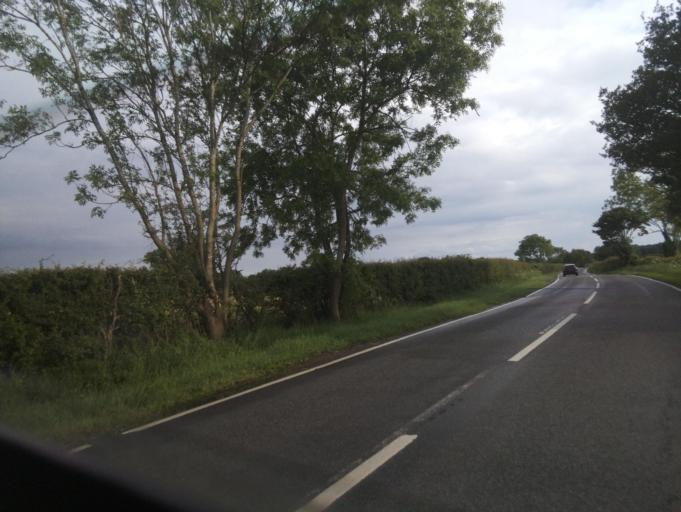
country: GB
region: England
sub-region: Lincolnshire
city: Great Gonerby
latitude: 53.0083
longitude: -0.6657
